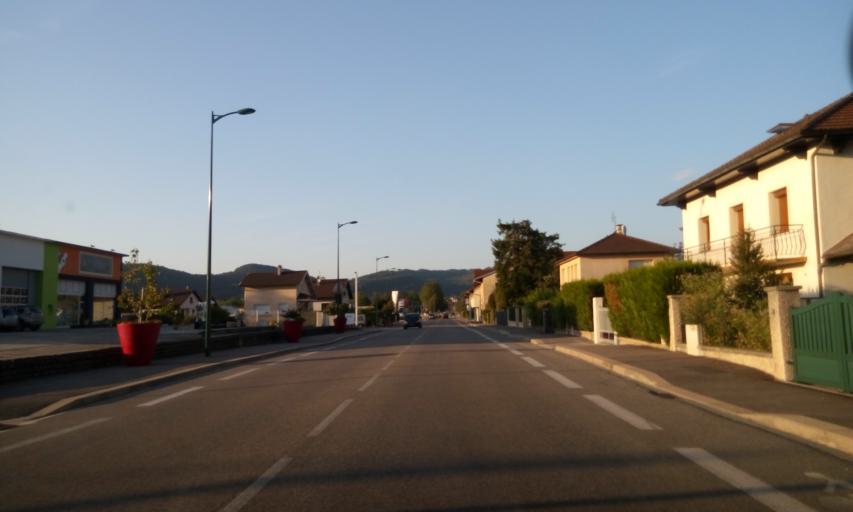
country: FR
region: Rhone-Alpes
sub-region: Departement de l'Ain
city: Montreal-la-Cluse
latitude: 46.1632
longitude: 5.5710
